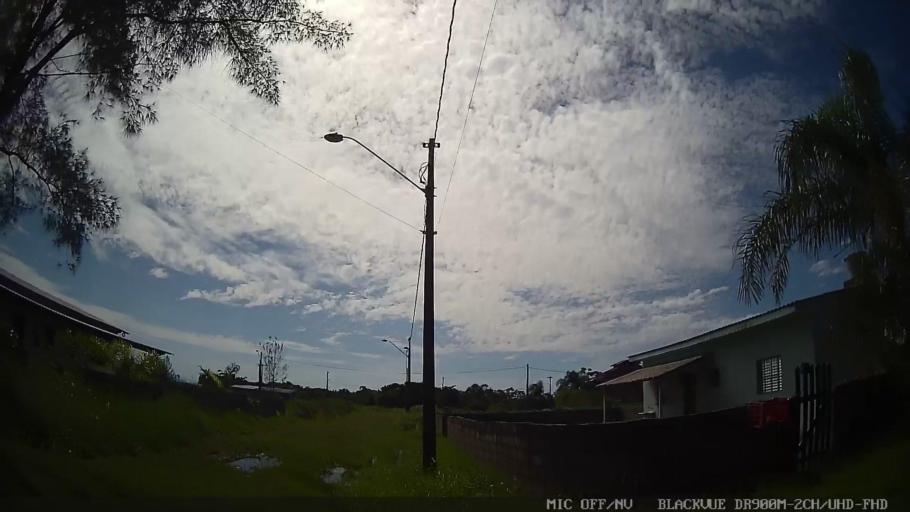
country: BR
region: Sao Paulo
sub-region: Iguape
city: Iguape
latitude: -24.7809
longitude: -47.6084
